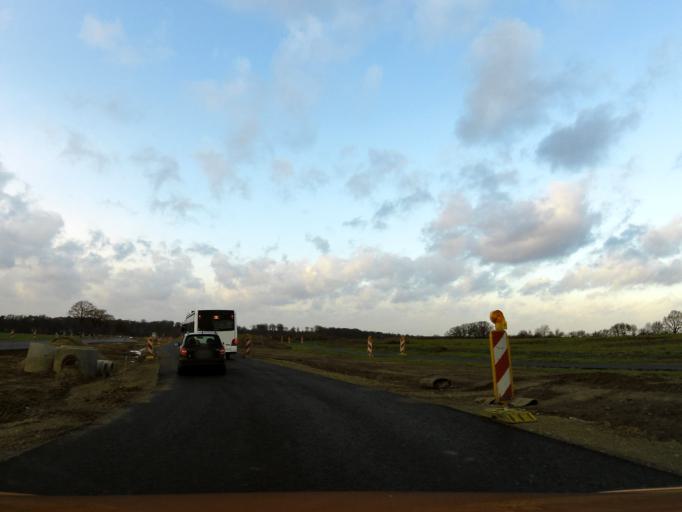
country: DE
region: Lower Saxony
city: Wolfsburg
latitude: 52.4112
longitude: 10.8226
